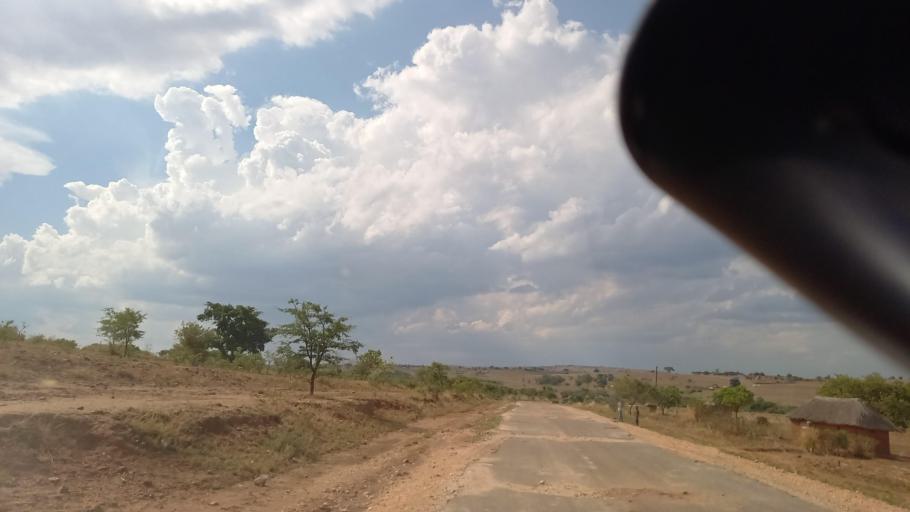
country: ZM
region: Lusaka
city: Kafue
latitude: -16.2147
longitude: 28.1134
